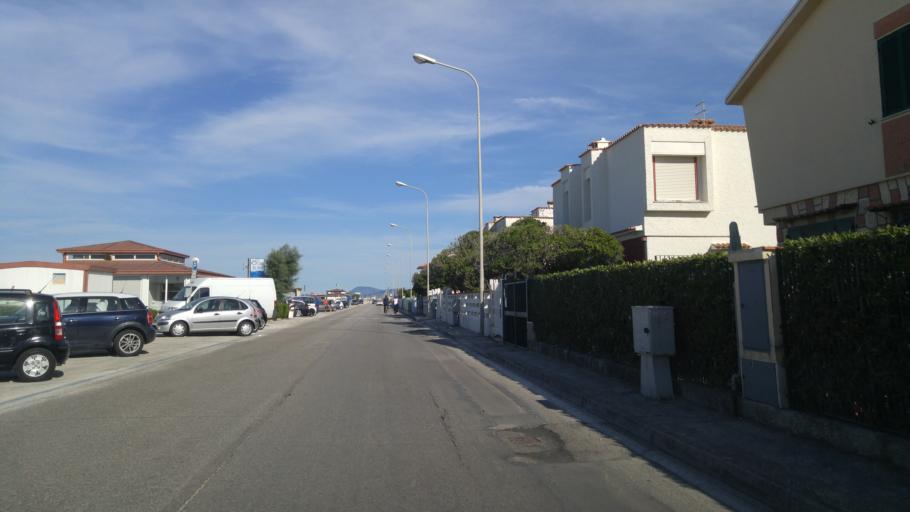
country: IT
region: The Marches
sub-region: Provincia di Ancona
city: Marina di Montemarciano
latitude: 43.6635
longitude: 13.3179
